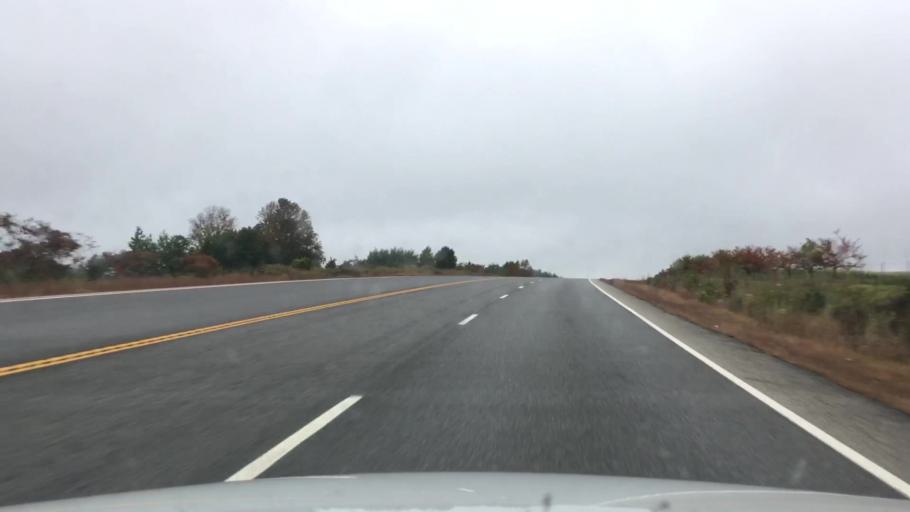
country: US
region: Maine
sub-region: Androscoggin County
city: Poland
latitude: 43.9823
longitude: -70.3681
